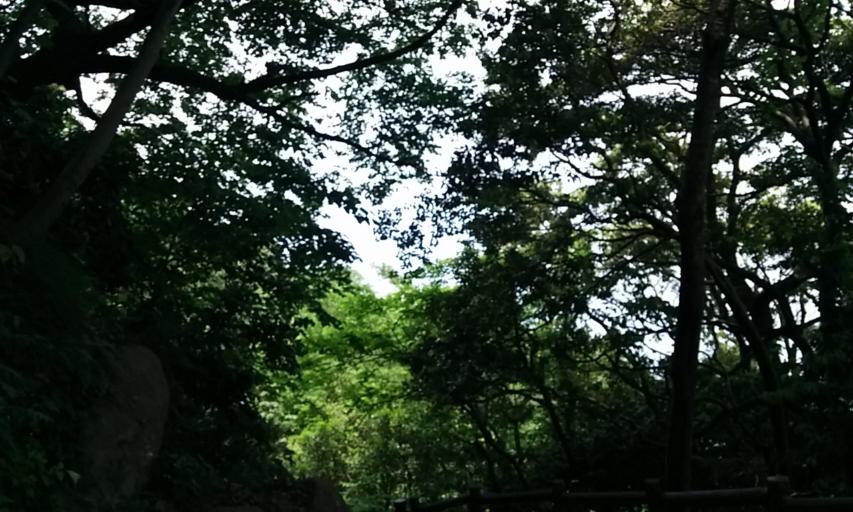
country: JP
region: Kyoto
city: Miyazu
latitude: 35.7757
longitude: 135.2238
